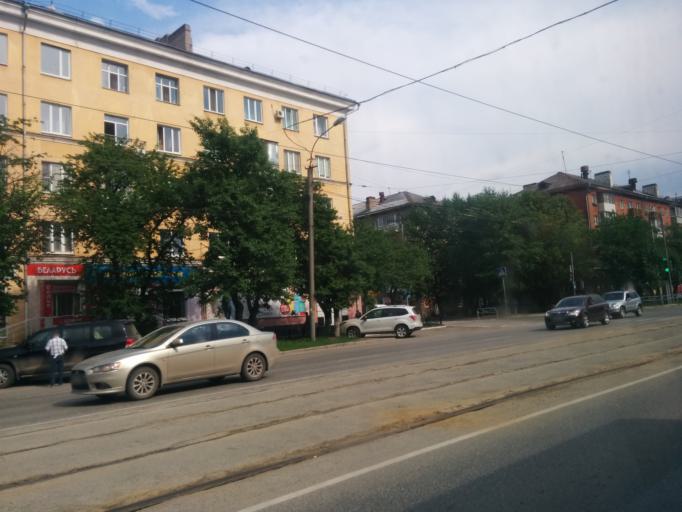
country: RU
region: Perm
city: Perm
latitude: 58.0181
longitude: 56.2782
